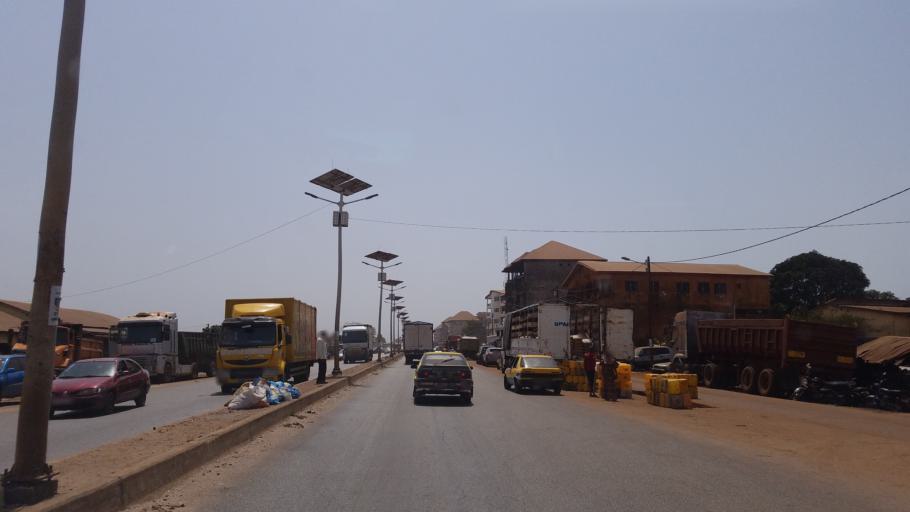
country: GN
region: Kindia
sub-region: Prefecture de Dubreka
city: Dubreka
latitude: 9.6558
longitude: -13.5720
